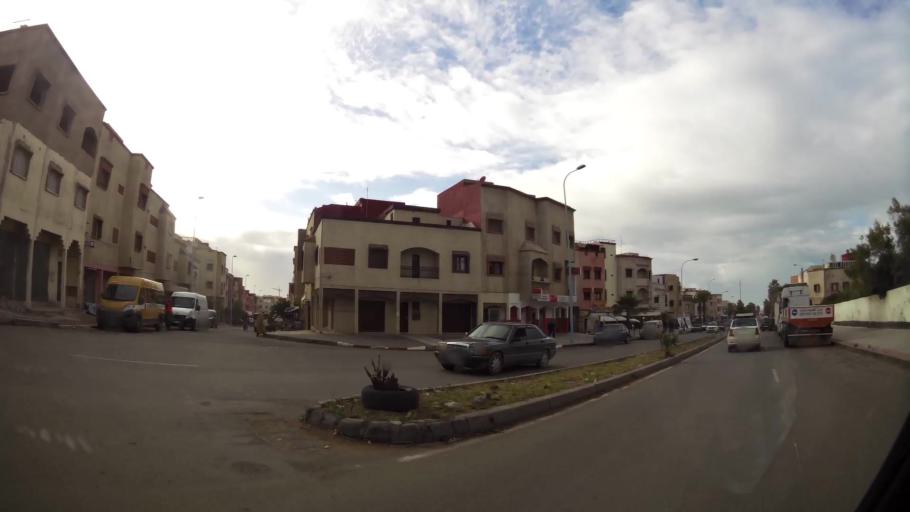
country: MA
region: Doukkala-Abda
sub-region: El-Jadida
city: El Jadida
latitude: 33.2523
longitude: -8.5180
